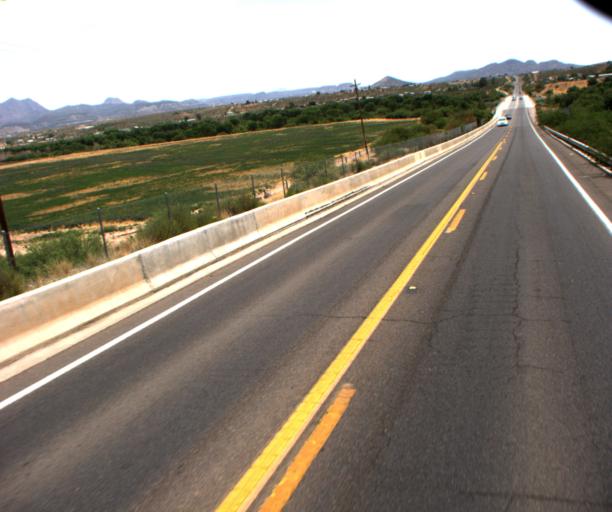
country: US
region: Arizona
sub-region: Gila County
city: Peridot
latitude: 33.2978
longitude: -110.4567
